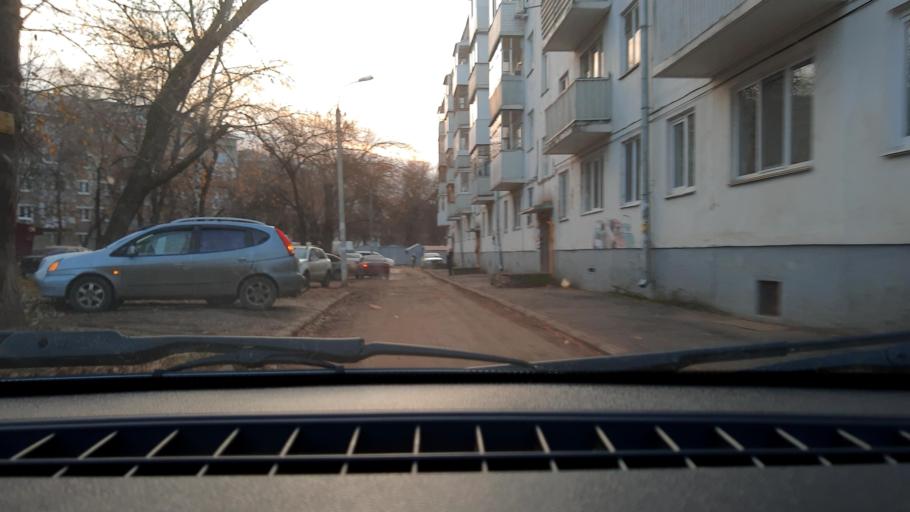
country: RU
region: Bashkortostan
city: Ufa
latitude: 54.8081
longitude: 56.1048
